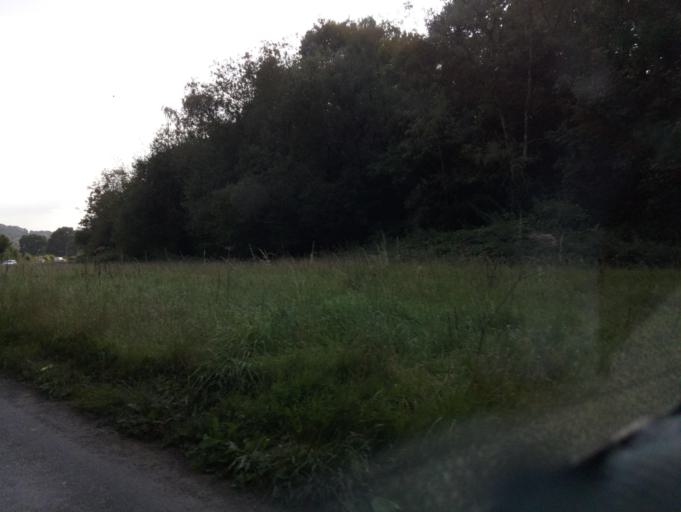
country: GB
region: England
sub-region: Devon
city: Tiverton
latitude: 50.8790
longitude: -3.4902
